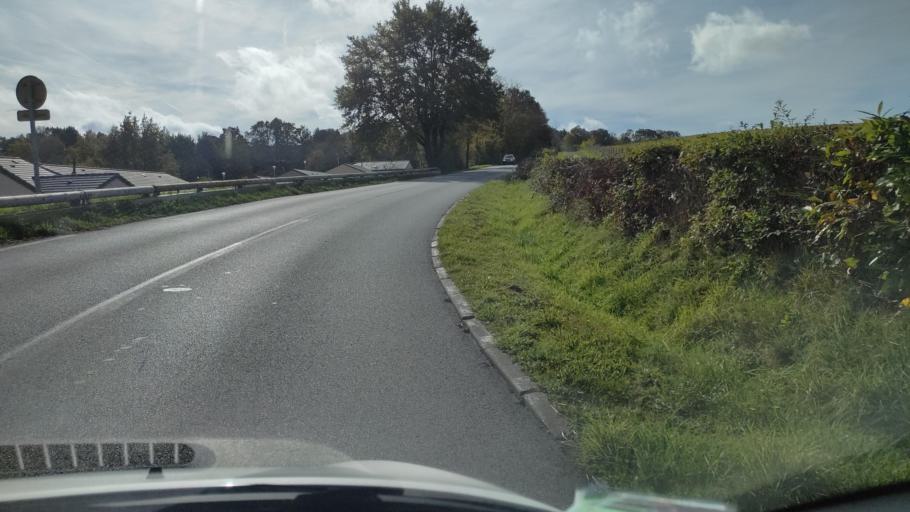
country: FR
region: Limousin
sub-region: Departement de la Haute-Vienne
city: Isle
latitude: 45.8160
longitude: 1.2150
